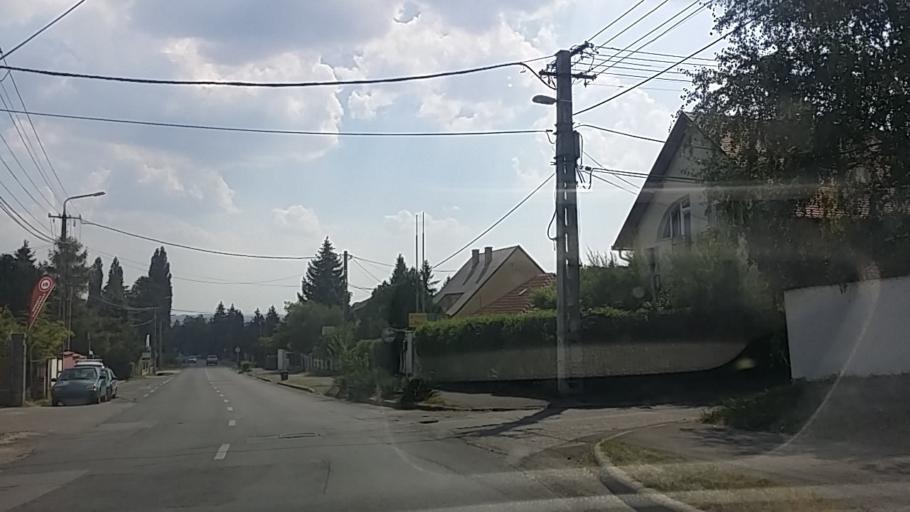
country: HU
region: Baranya
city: Pecs
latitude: 46.0769
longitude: 18.1871
